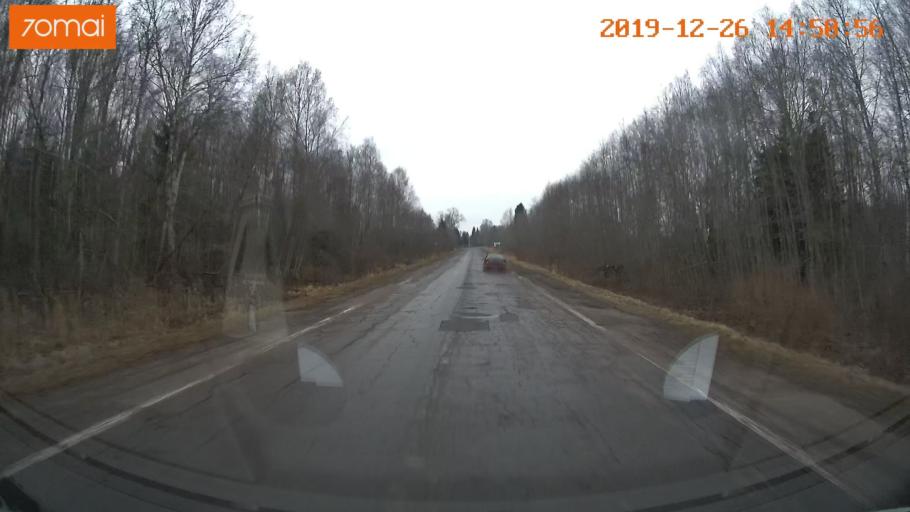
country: RU
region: Jaroslavl
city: Poshekhon'ye
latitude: 58.3284
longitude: 38.9177
